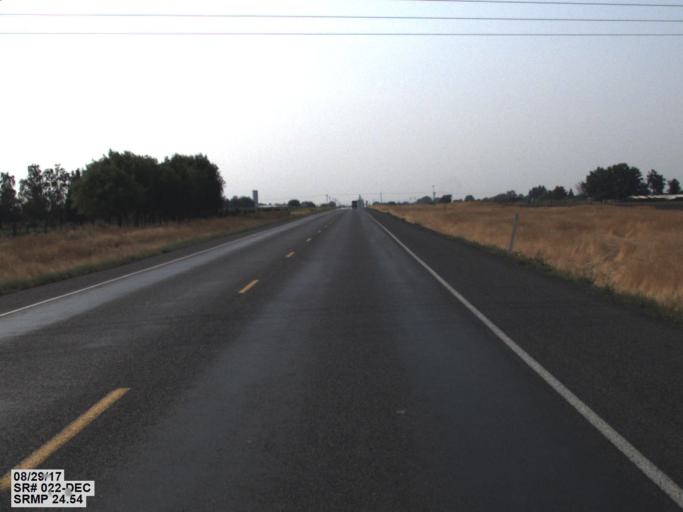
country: US
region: Washington
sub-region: Yakima County
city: Mabton
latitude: 46.2048
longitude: -119.9715
